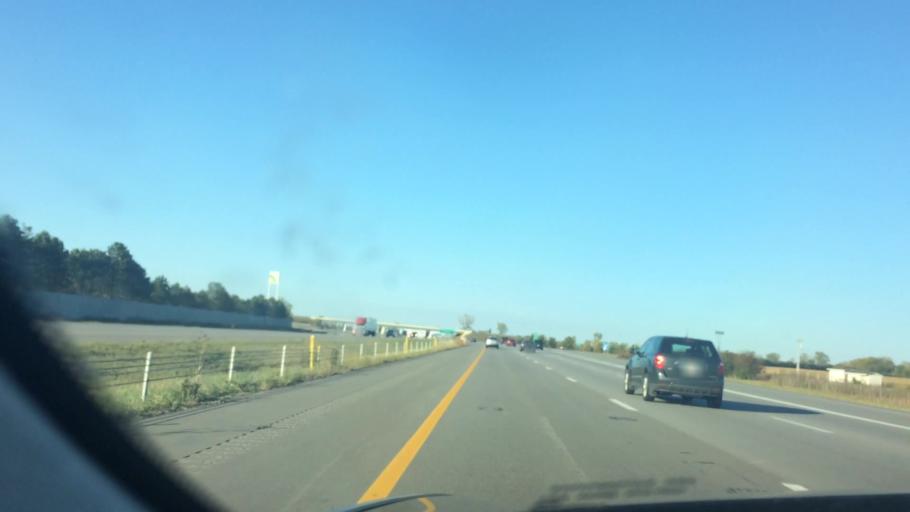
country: US
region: Ohio
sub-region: Wood County
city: Bowling Green
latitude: 41.3694
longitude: -83.6170
